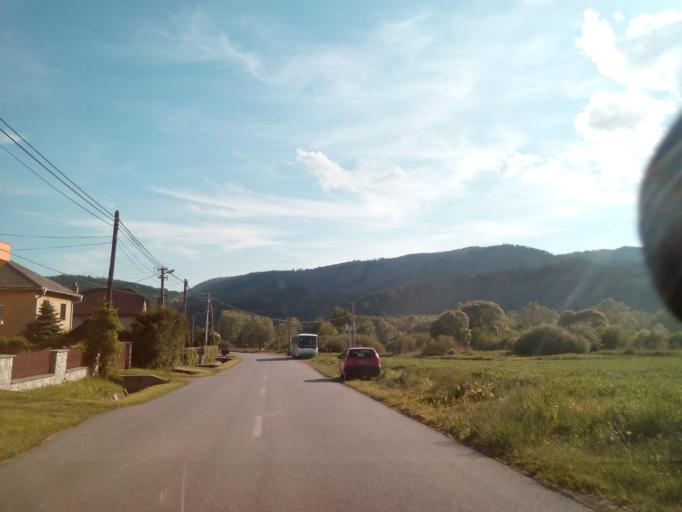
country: SK
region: Presovsky
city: Lipany
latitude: 49.0514
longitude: 20.9494
